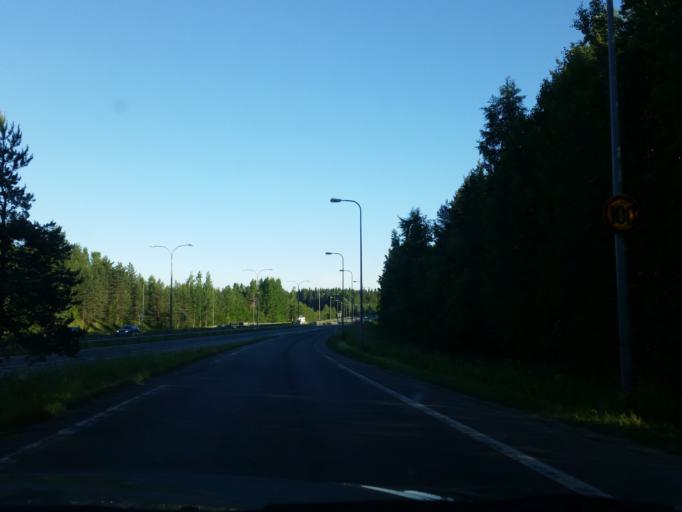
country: FI
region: Northern Savo
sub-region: Kuopio
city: Kuopio
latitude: 62.8611
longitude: 27.6179
